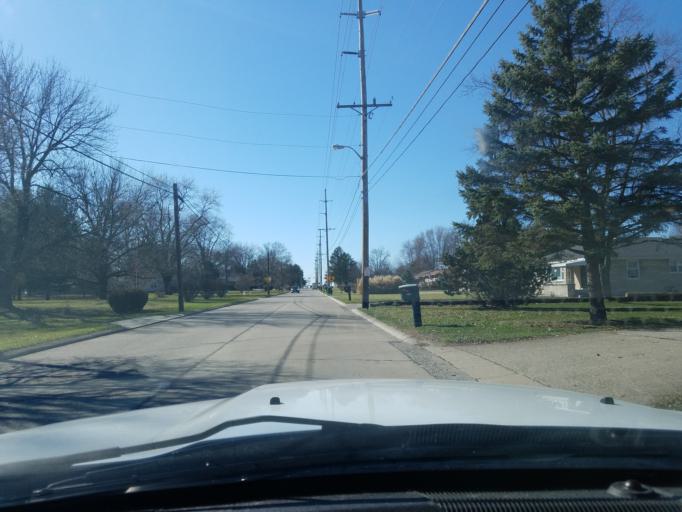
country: US
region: Indiana
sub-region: Shelby County
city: Shelbyville
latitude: 39.5046
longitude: -85.7684
